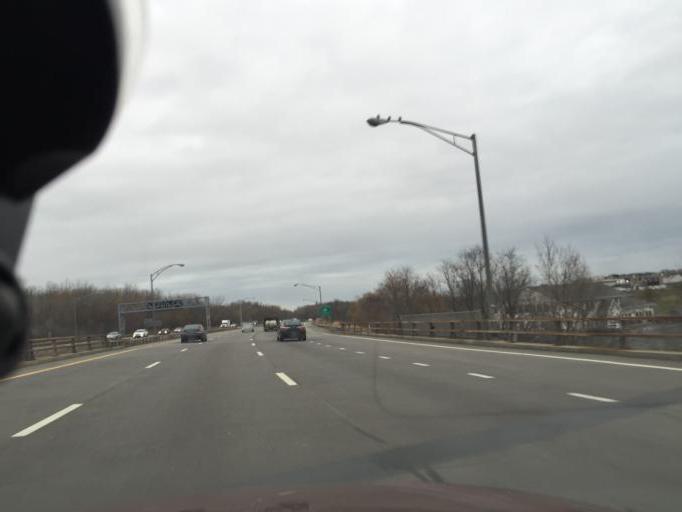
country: US
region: New York
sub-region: Monroe County
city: Greece
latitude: 43.1956
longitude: -77.6821
